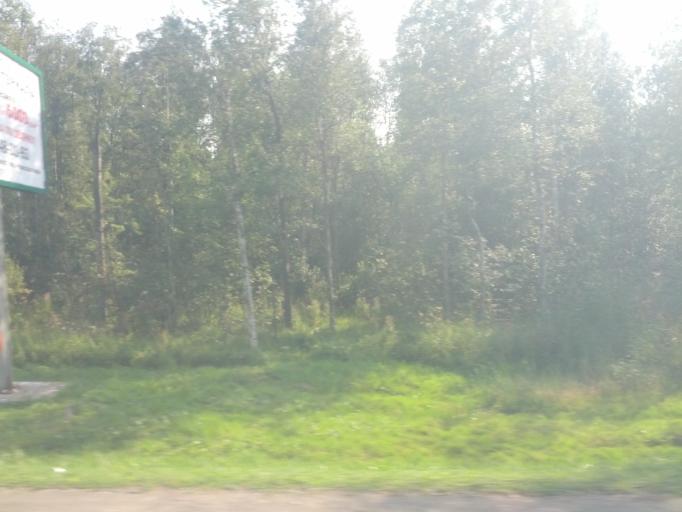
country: RU
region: Leningrad
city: Yanino Vtoroye
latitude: 59.8906
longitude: 30.5642
